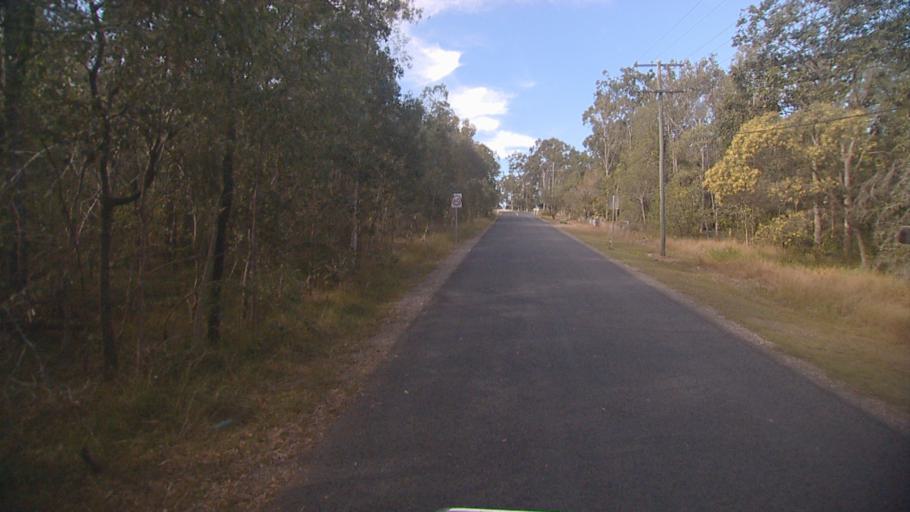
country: AU
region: Queensland
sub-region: Logan
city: North Maclean
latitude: -27.7771
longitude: 152.9687
